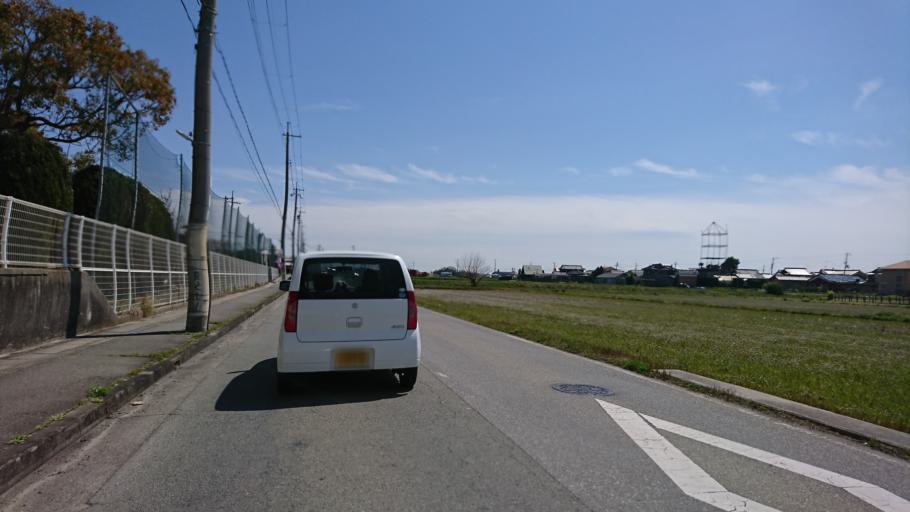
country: JP
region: Hyogo
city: Kakogawacho-honmachi
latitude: 34.7408
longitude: 134.8937
